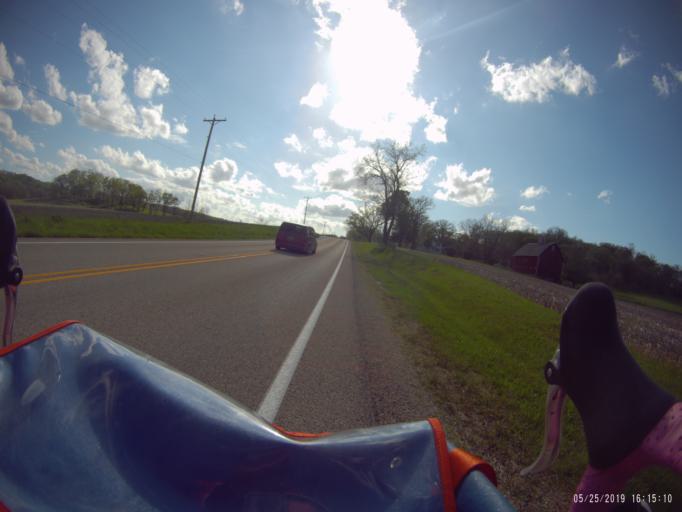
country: US
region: Wisconsin
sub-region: Dane County
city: Mount Horeb
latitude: 42.9638
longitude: -89.6837
